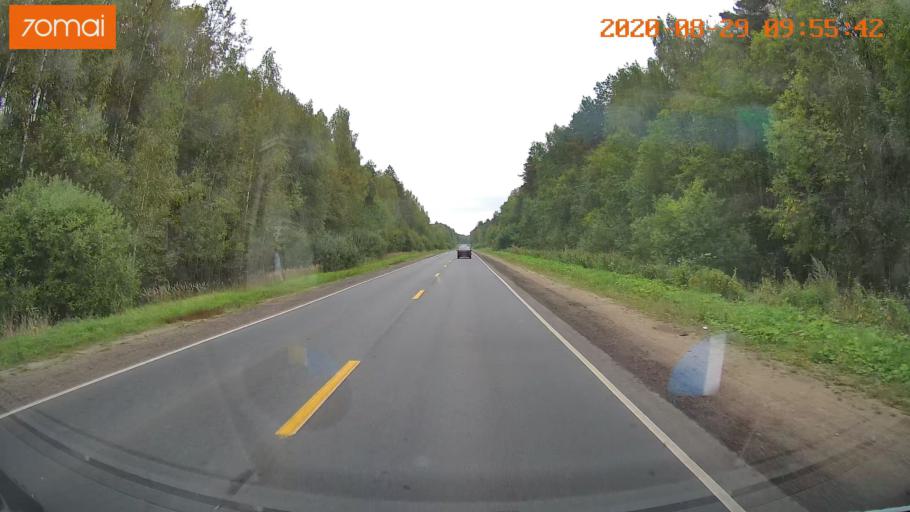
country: RU
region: Ivanovo
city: Zarechnyy
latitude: 57.4219
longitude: 42.2701
